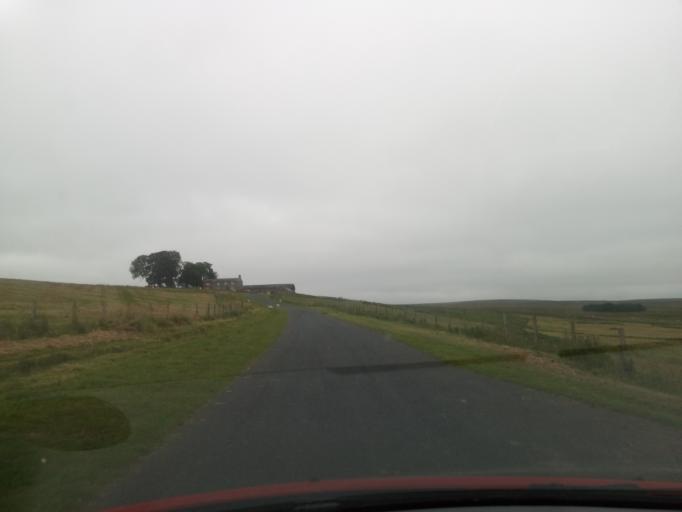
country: GB
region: England
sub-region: Northumberland
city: Rochester
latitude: 55.2929
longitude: -2.2068
